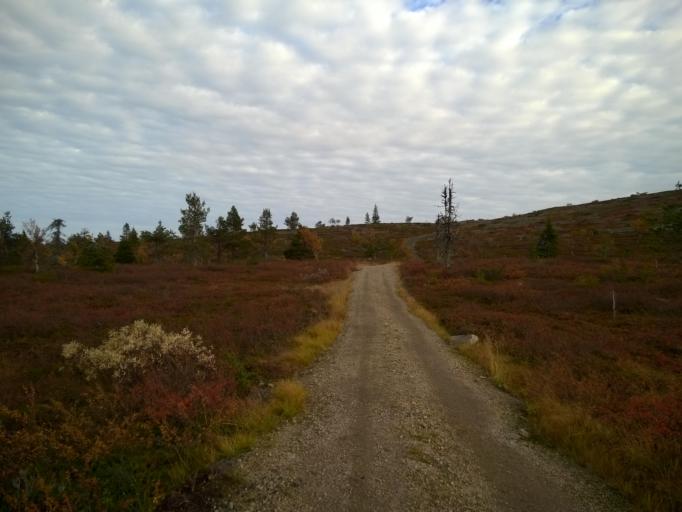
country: FI
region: Lapland
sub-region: Tunturi-Lappi
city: Muonio
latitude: 67.9813
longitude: 24.1157
